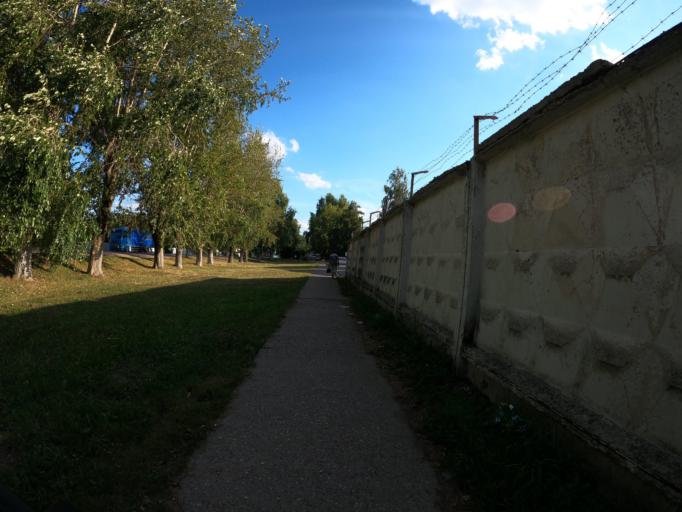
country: RU
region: Moskovskaya
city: Raduzhnyy
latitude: 55.1388
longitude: 38.7311
